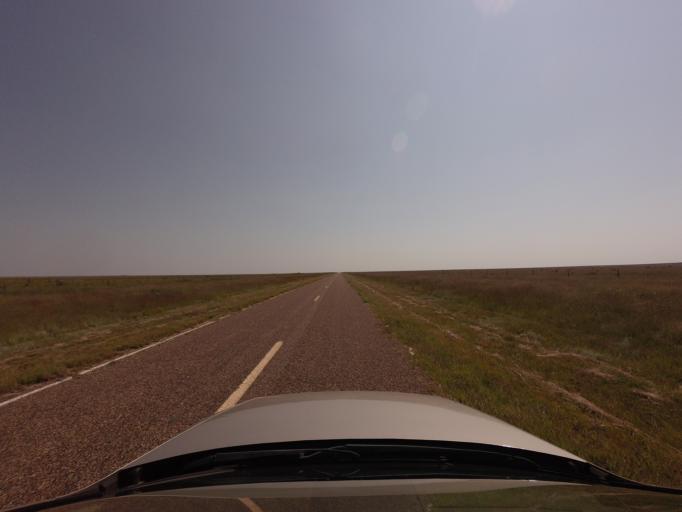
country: US
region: New Mexico
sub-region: Curry County
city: Cannon Air Force Base
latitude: 34.6334
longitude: -103.4746
